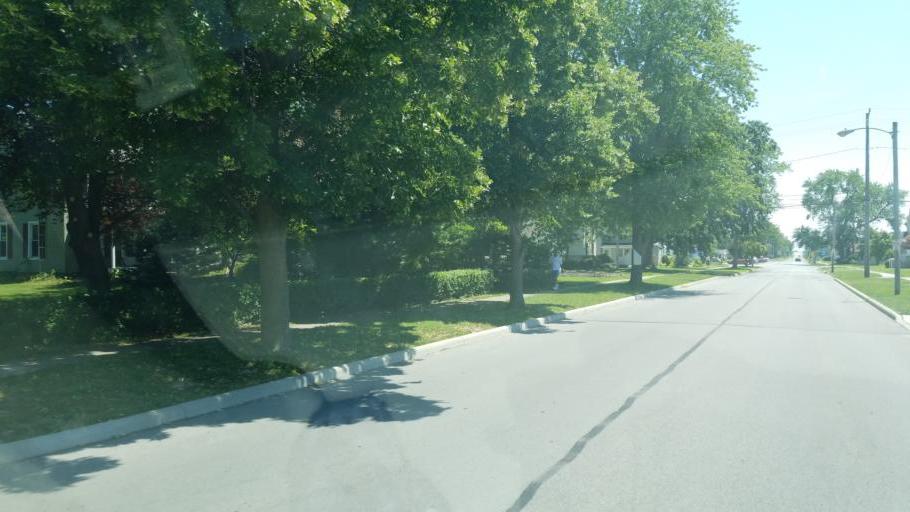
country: US
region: Ohio
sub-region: Ottawa County
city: Port Clinton
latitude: 41.5078
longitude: -82.9338
